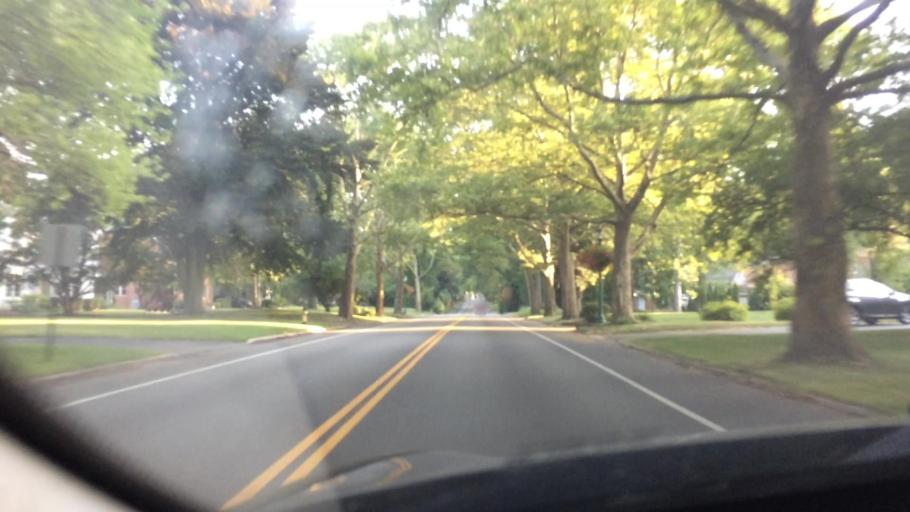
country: US
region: Ohio
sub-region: Lucas County
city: Ottawa Hills
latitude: 41.6689
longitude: -83.6437
